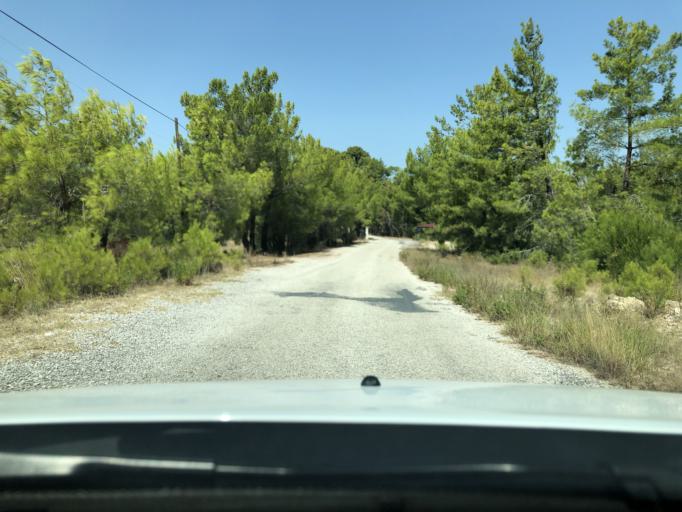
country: TR
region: Antalya
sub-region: Manavgat
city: Manavgat
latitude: 36.8428
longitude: 31.5295
